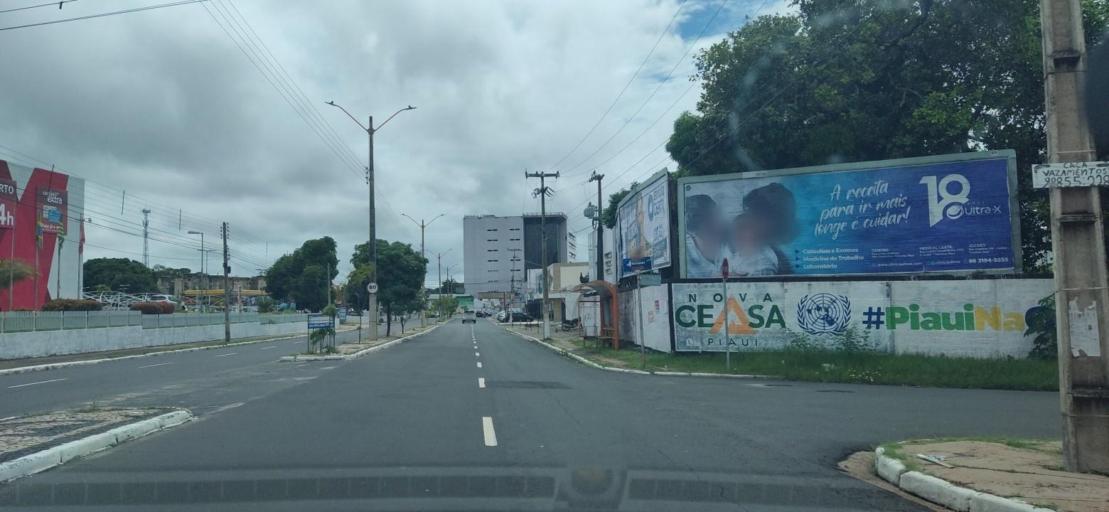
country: BR
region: Piaui
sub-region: Teresina
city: Teresina
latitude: -5.0722
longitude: -42.7741
